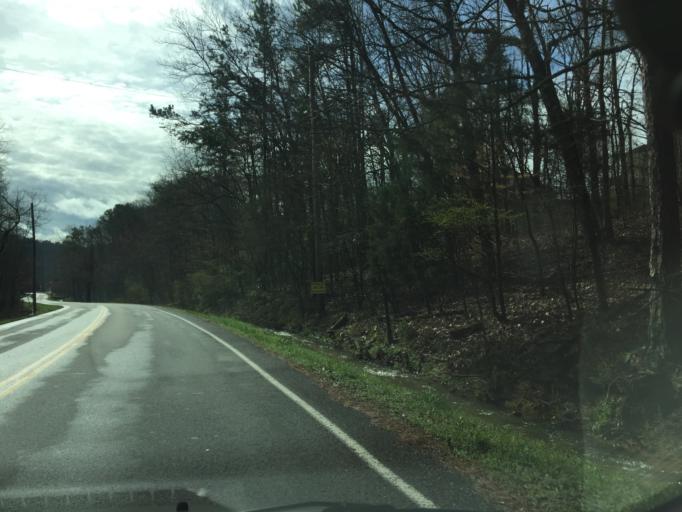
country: US
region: Tennessee
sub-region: Hamilton County
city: Collegedale
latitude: 35.0189
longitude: -85.0959
